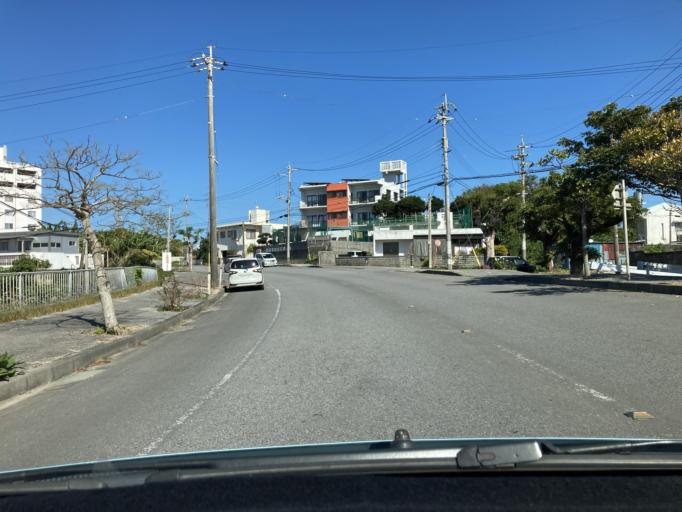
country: JP
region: Okinawa
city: Gushikawa
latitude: 26.3817
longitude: 127.8691
